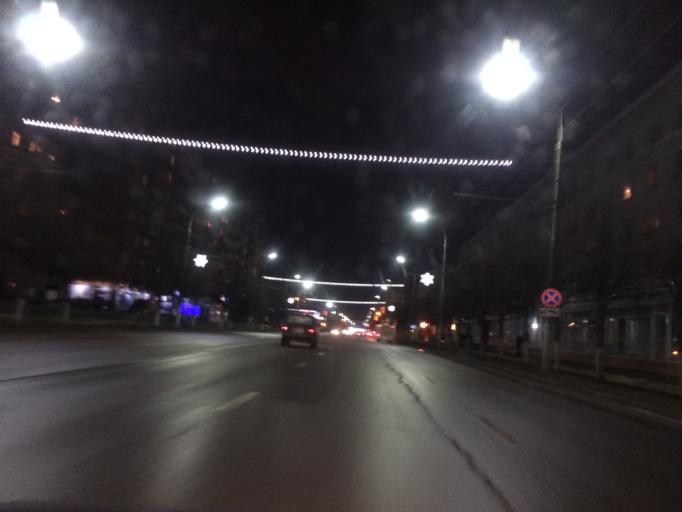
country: RU
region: Tula
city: Tula
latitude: 54.1973
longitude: 37.5977
